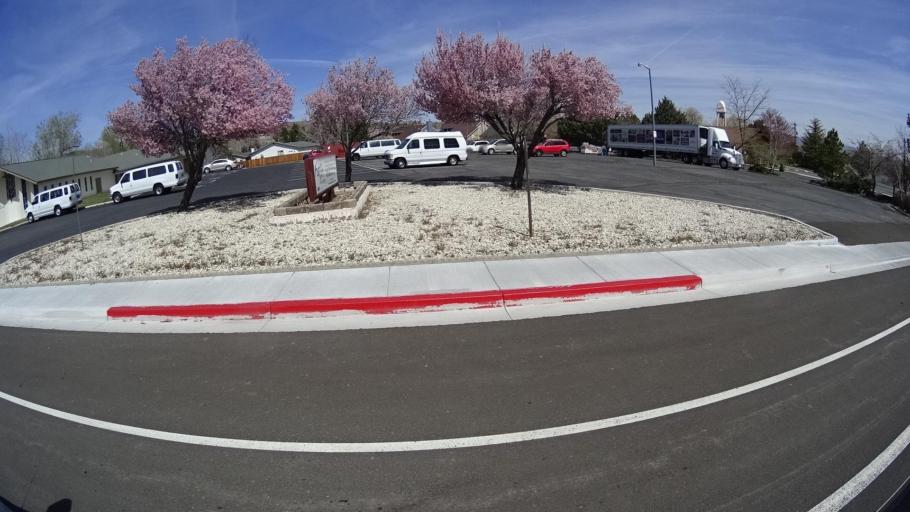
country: US
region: Nevada
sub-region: Washoe County
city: Reno
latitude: 39.5370
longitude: -119.8446
